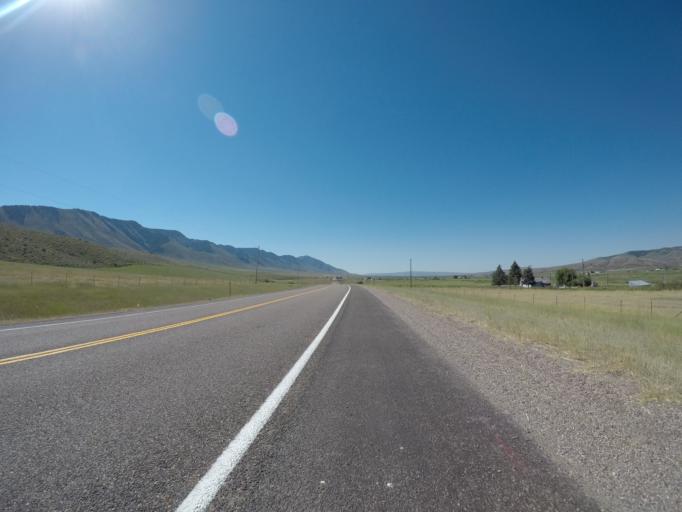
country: US
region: Idaho
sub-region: Bear Lake County
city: Montpelier
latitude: 42.3709
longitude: -111.0532
